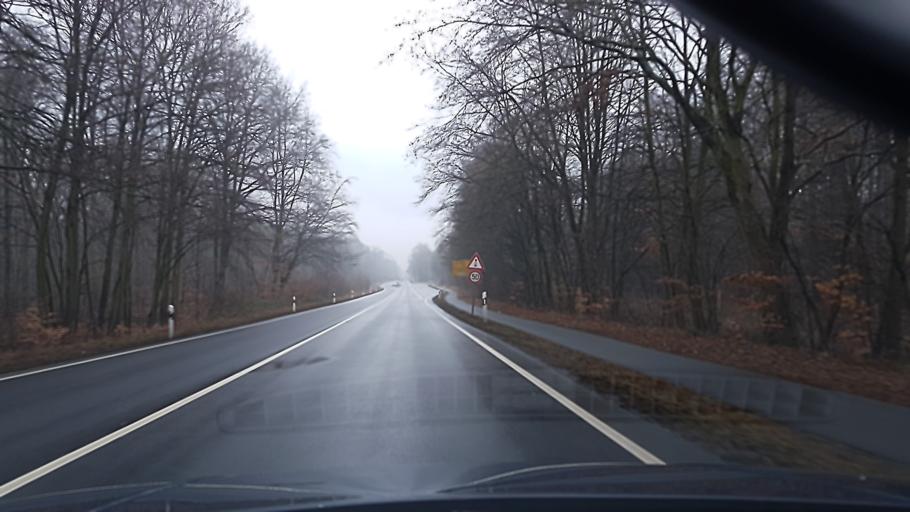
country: DE
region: Lower Saxony
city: Leiferde
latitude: 52.1798
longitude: 10.4531
